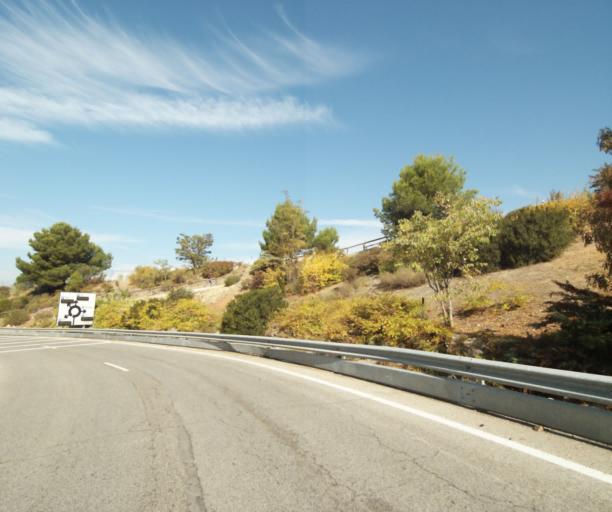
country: FR
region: Provence-Alpes-Cote d'Azur
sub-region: Departement des Bouches-du-Rhone
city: Saint-Victoret
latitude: 43.4340
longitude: 5.2361
